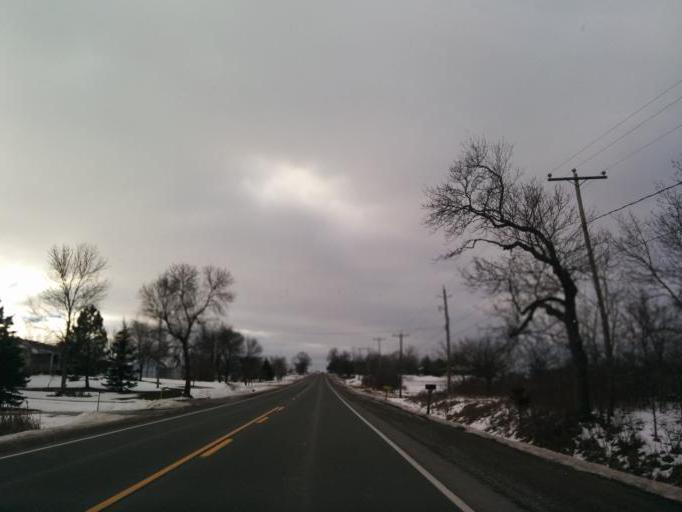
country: CA
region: Ontario
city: Ancaster
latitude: 42.9465
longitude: -79.8714
